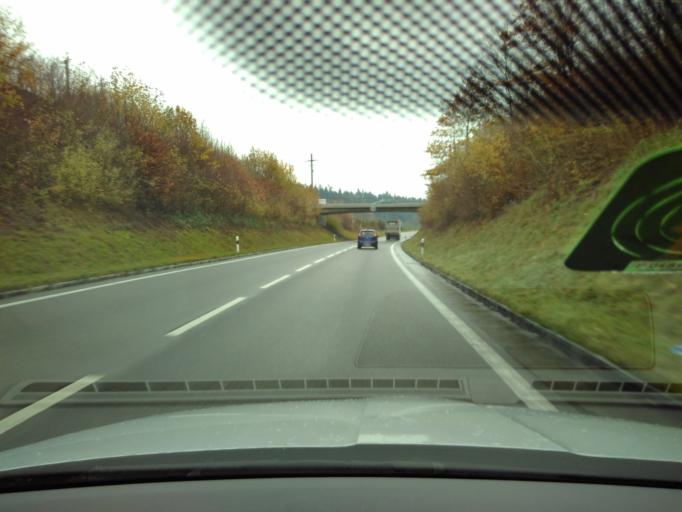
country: CH
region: Aargau
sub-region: Bezirk Kulm
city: Schoftland
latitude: 47.3018
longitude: 8.0432
